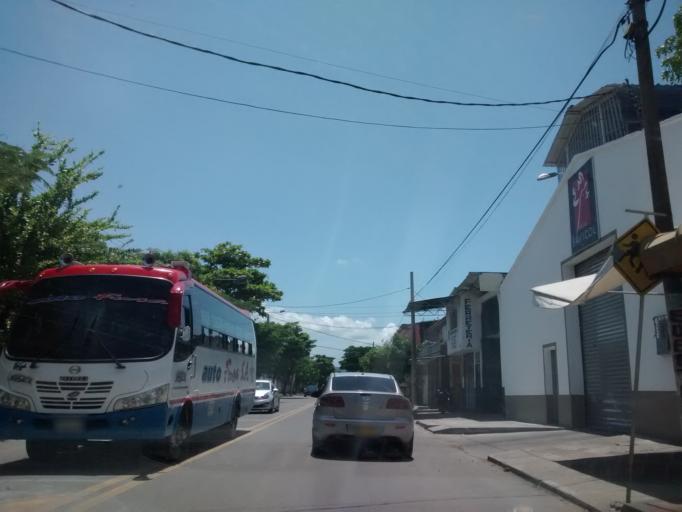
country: CO
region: Cundinamarca
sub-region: Girardot
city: Girardot City
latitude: 4.3004
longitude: -74.8006
